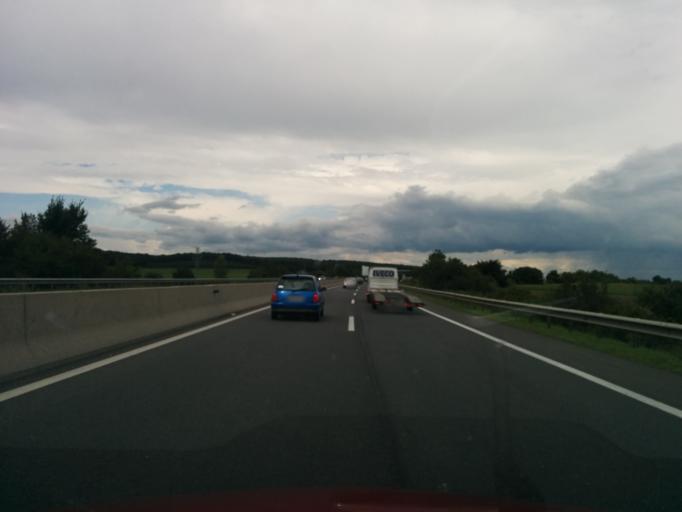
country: AT
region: Burgenland
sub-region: Politischer Bezirk Neusiedl am See
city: Parndorf
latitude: 47.9849
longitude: 16.8357
